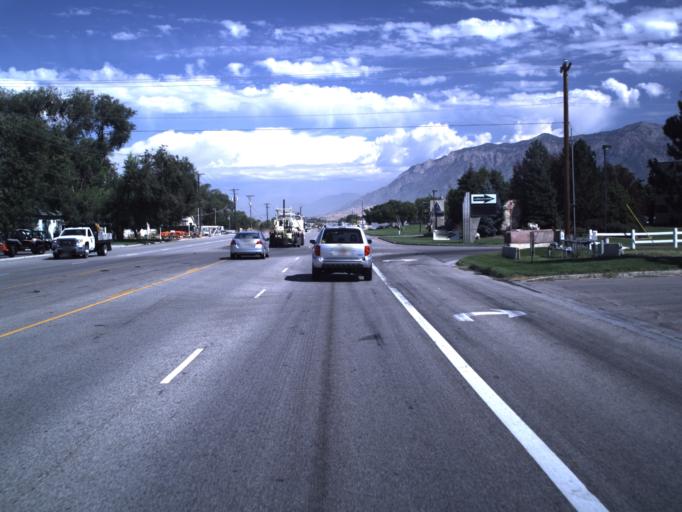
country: US
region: Utah
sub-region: Weber County
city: Marriott-Slaterville
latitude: 41.2237
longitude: -112.0256
